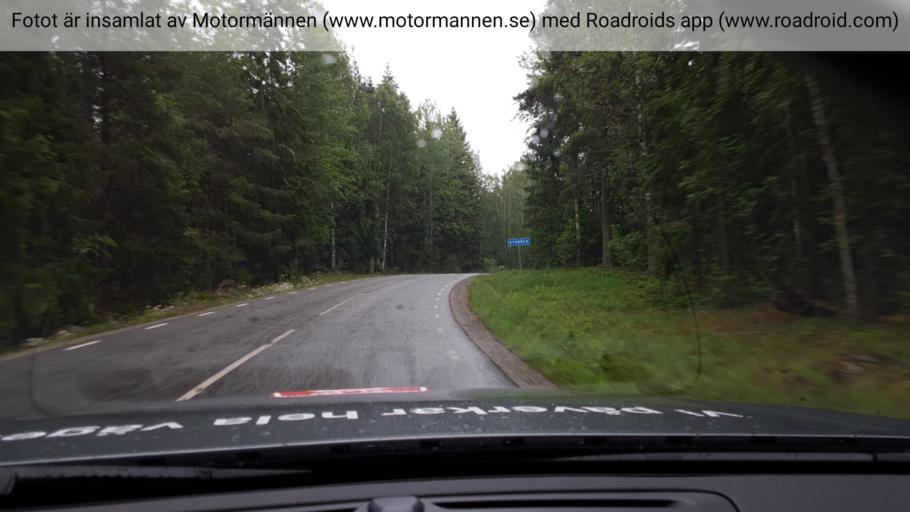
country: SE
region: Vaestmanland
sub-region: Norbergs Kommun
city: Norberg
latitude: 59.9753
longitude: 16.0223
